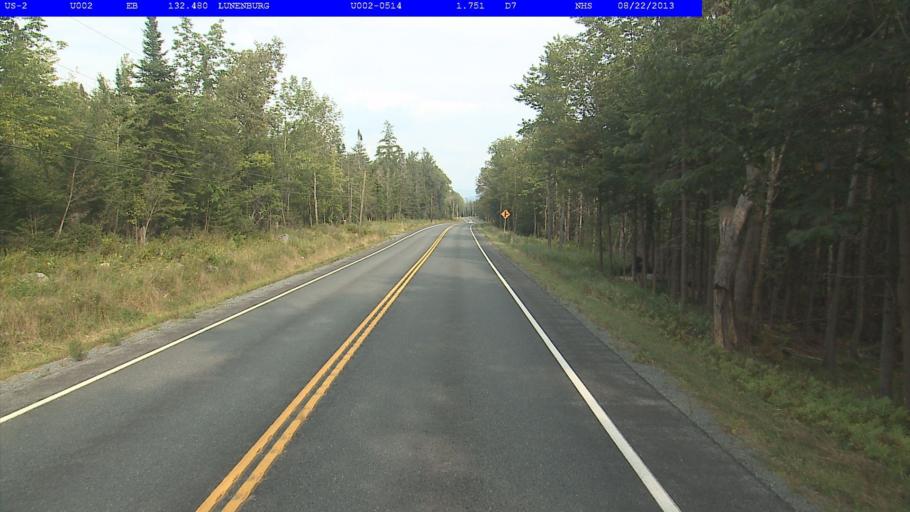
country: US
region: New Hampshire
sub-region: Coos County
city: Whitefield
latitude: 44.4647
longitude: -71.7408
